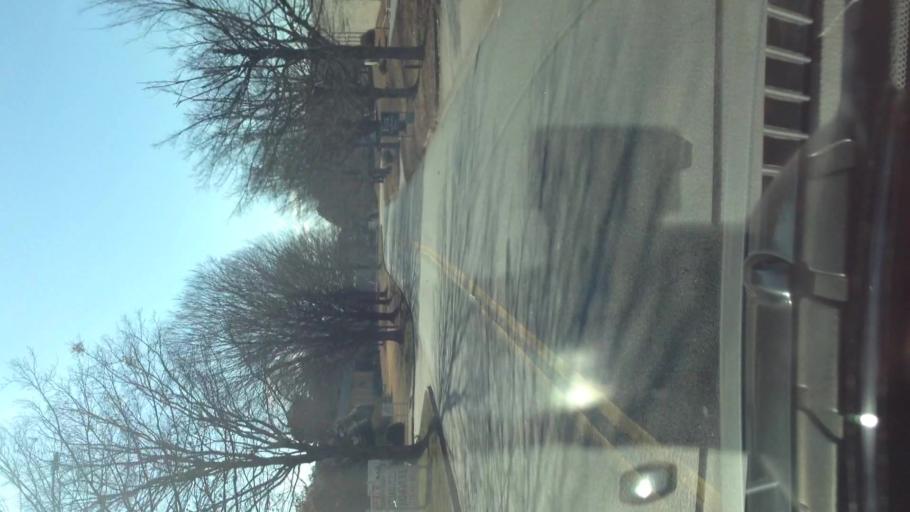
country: US
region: Georgia
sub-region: DeKalb County
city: Doraville
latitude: 33.9267
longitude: -84.2593
